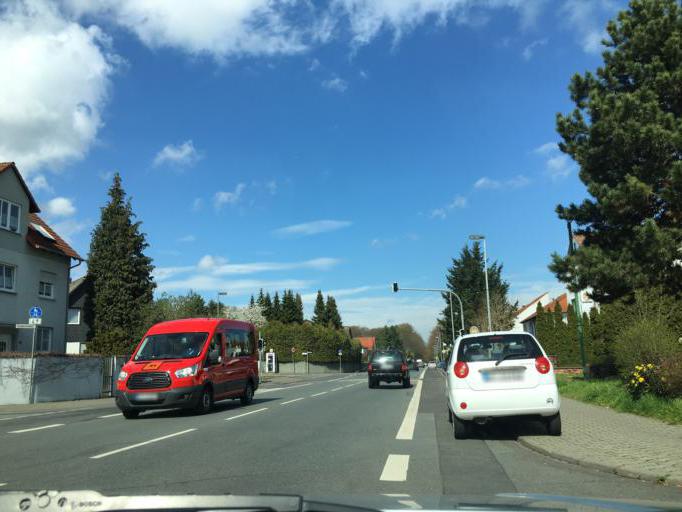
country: DE
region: Hesse
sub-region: Regierungsbezirk Darmstadt
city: Dietzenbach
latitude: 50.0301
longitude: 8.7871
